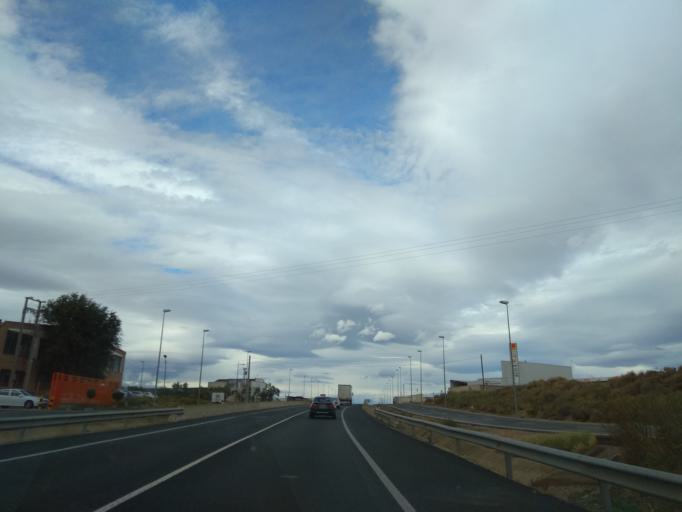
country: ES
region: La Rioja
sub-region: Provincia de La Rioja
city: Alfaro
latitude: 42.1563
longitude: -1.7255
